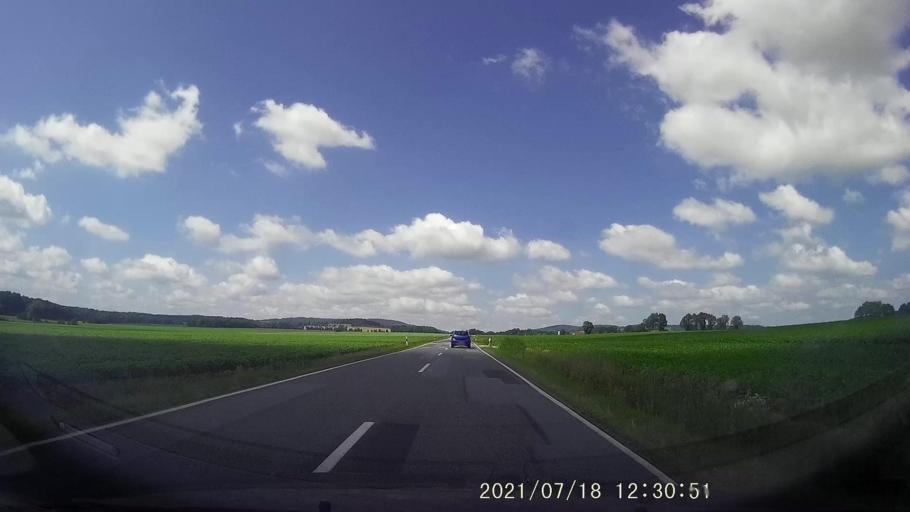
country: DE
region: Saxony
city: Konigshain
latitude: 51.1746
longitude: 14.9044
